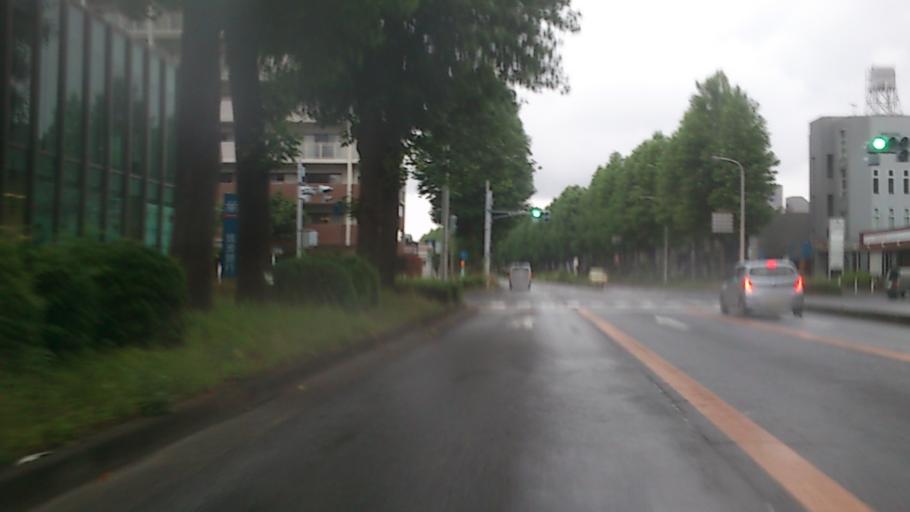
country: JP
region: Ibaraki
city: Naka
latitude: 36.0621
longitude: 140.1195
